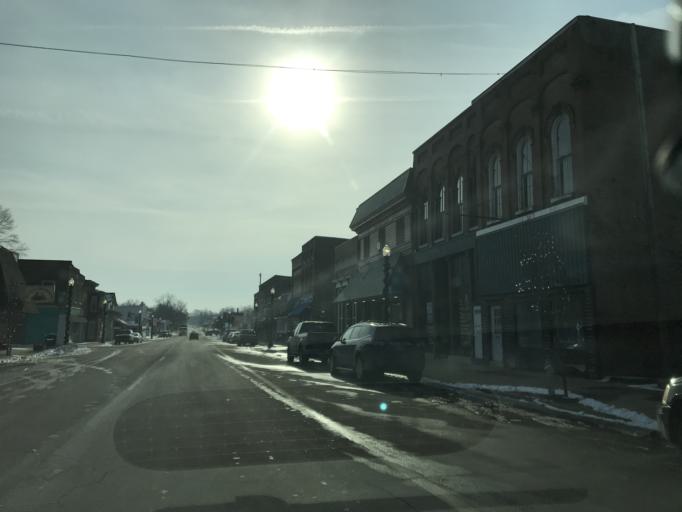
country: US
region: Michigan
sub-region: Barry County
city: Nashville
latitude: 42.6045
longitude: -85.0936
